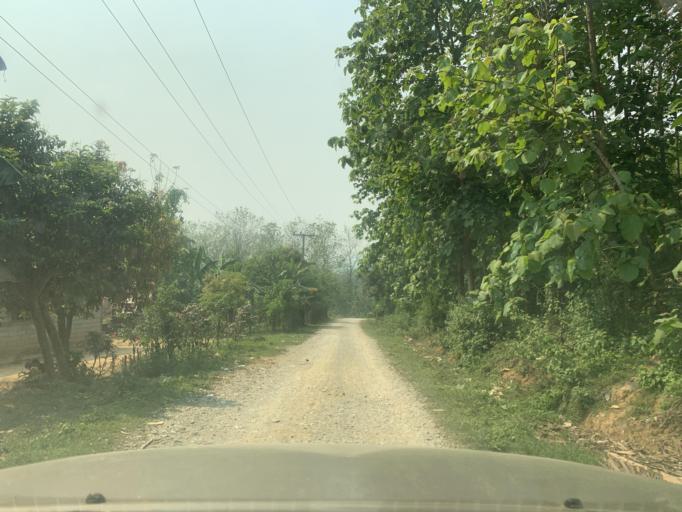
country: LA
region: Louangphabang
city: Louangphabang
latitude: 19.8846
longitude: 102.2530
